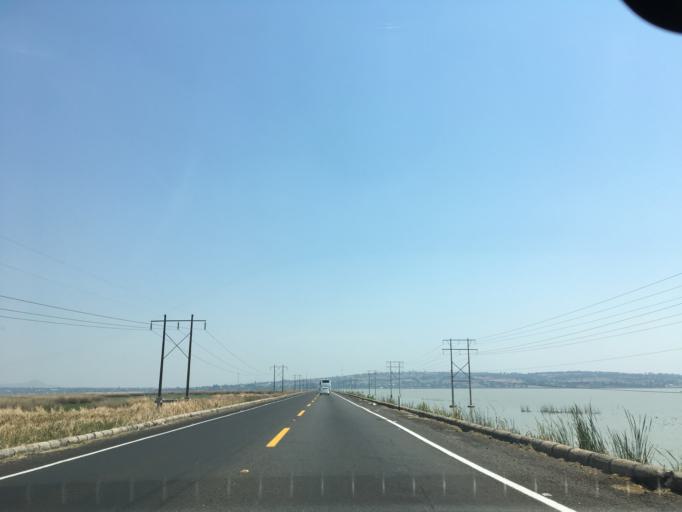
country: MX
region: Michoacan
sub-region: Cuitzeo
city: San Juan Benito Juarez (San Juan Tararameo)
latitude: 19.9344
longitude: -101.1390
